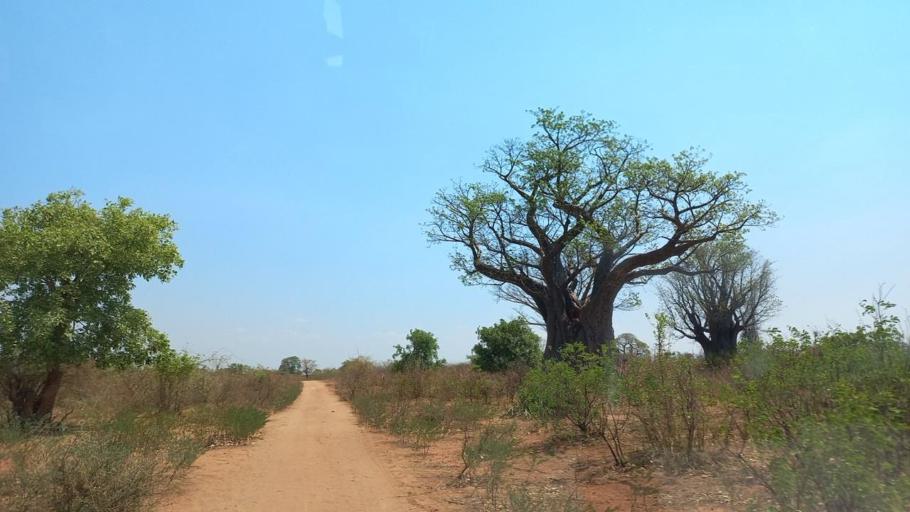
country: ZM
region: Lusaka
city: Luangwa
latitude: -15.5986
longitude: 30.4018
